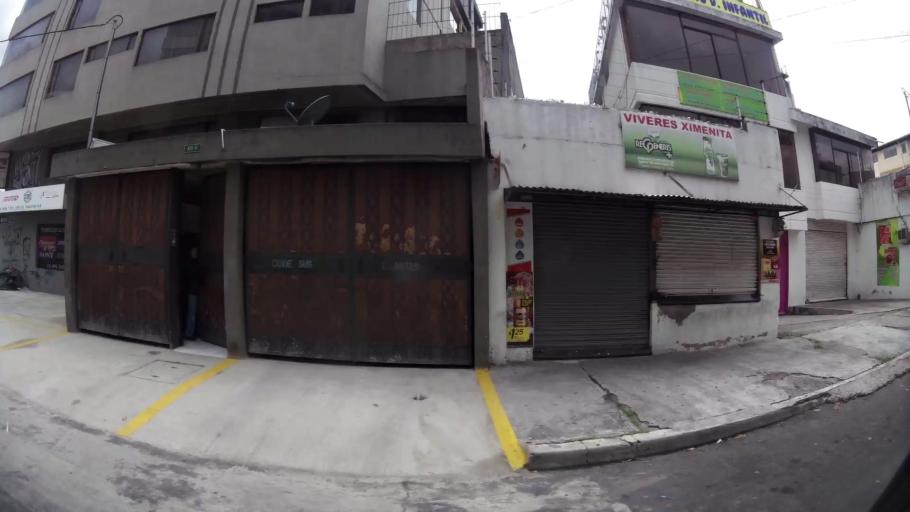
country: EC
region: Pichincha
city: Quito
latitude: -0.1725
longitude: -78.4763
